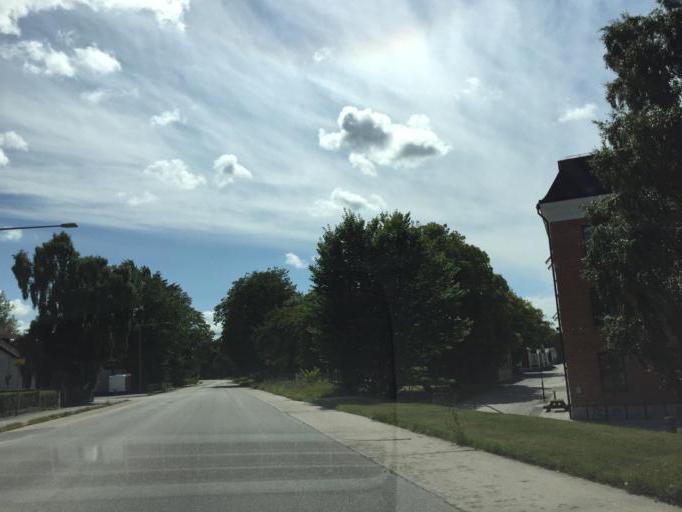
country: SE
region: Gotland
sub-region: Gotland
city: Visby
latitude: 57.6141
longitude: 18.2848
